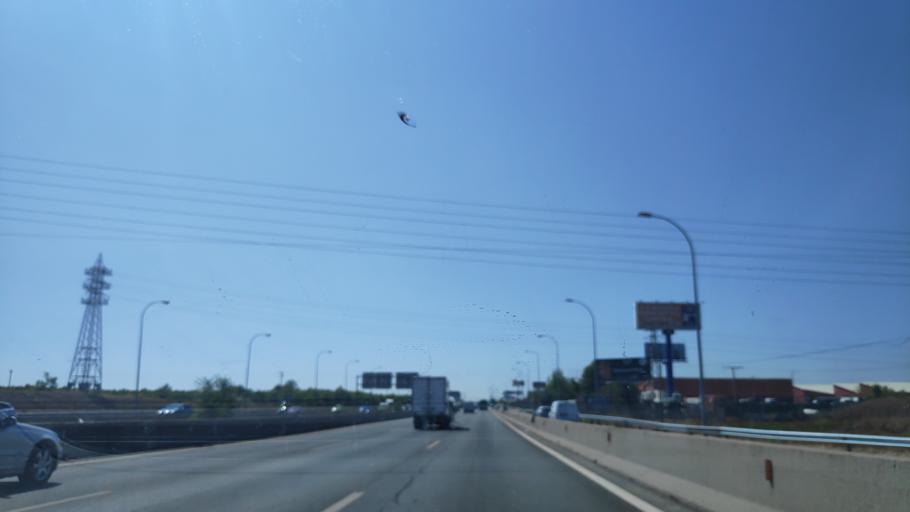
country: ES
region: Madrid
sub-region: Provincia de Madrid
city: Villaverde
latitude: 40.3622
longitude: -3.7212
